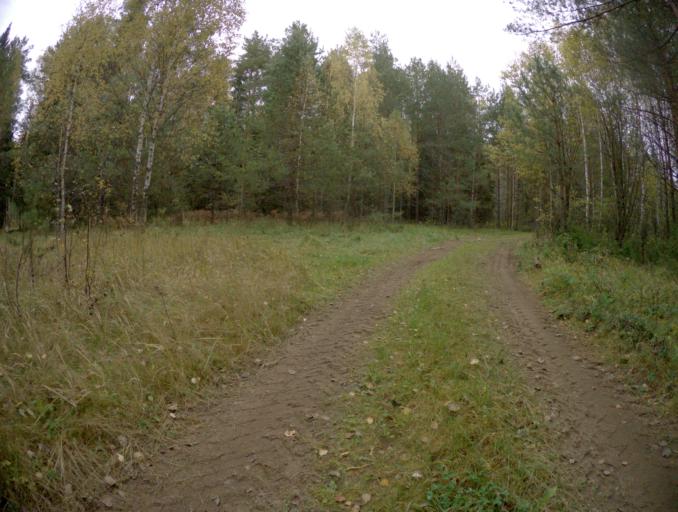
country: RU
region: Vladimir
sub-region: Kovrovskiy Rayon
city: Kovrov
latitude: 56.3339
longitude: 41.4698
